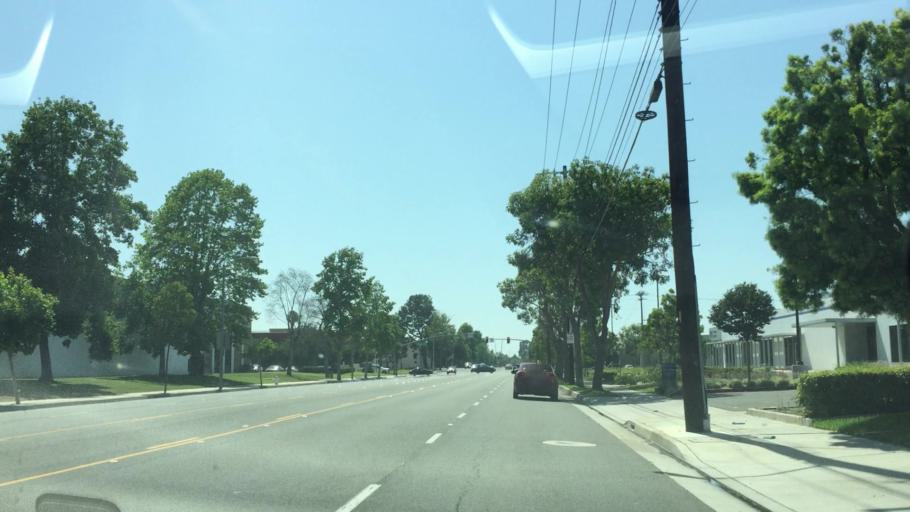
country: US
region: California
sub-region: Orange County
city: Fountain Valley
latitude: 33.7088
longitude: -117.9108
